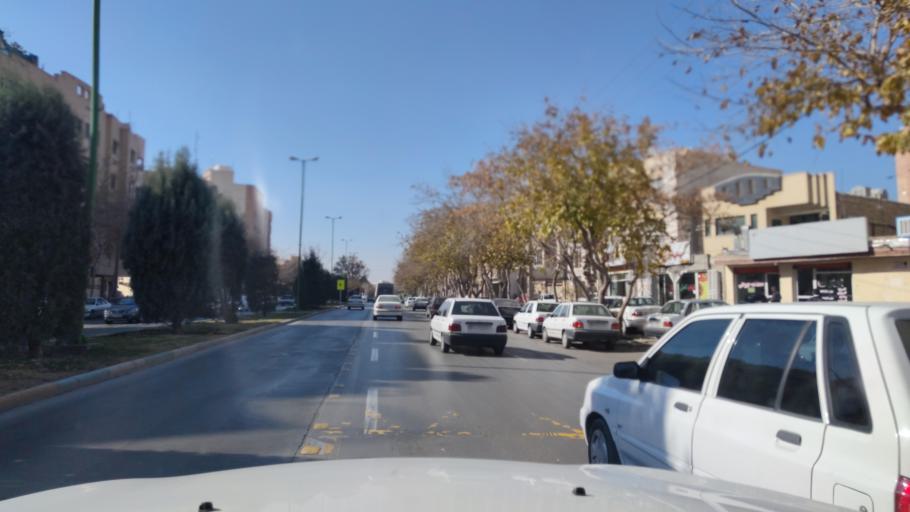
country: IR
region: Isfahan
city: Isfahan
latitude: 32.6802
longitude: 51.6548
